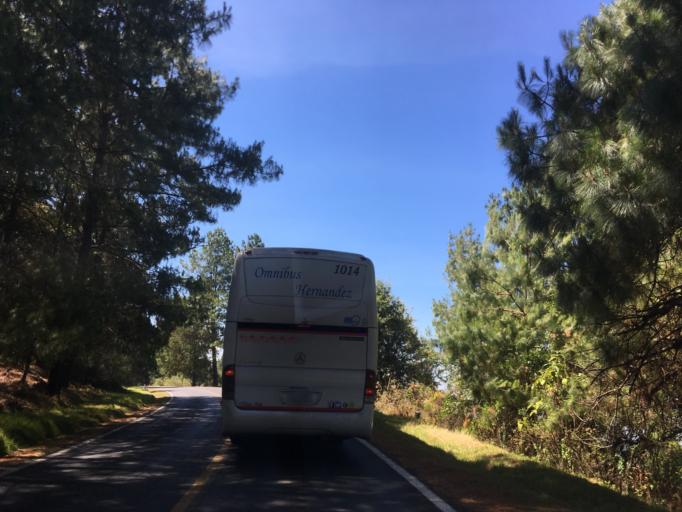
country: MX
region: Michoacan
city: Tzitzio
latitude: 19.6783
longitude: -100.8613
